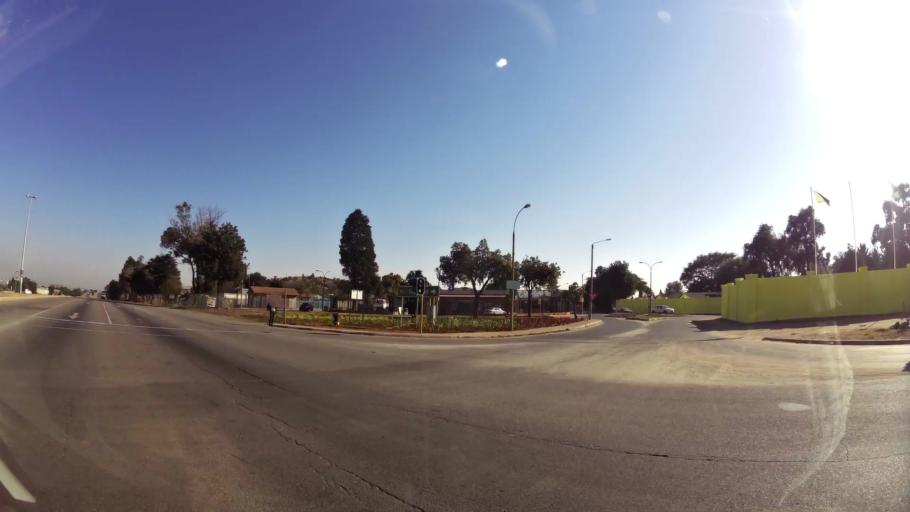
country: ZA
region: Gauteng
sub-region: City of Johannesburg Metropolitan Municipality
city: Modderfontein
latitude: -26.0600
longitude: 28.1772
